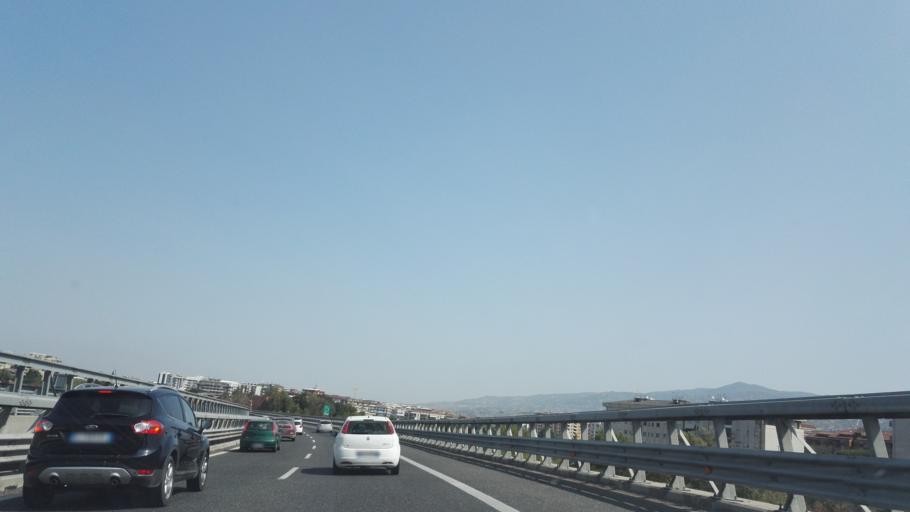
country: IT
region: Calabria
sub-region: Provincia di Cosenza
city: Cosenza
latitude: 39.3157
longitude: 16.2414
